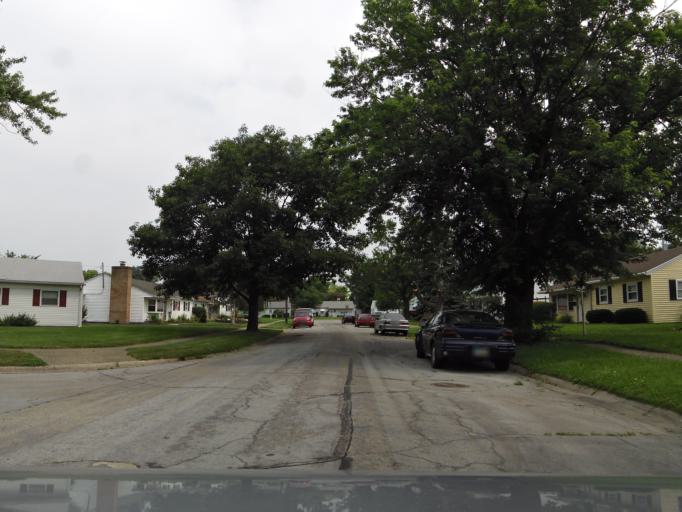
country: US
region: Ohio
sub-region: Montgomery County
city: Riverside
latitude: 39.7347
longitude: -84.1229
